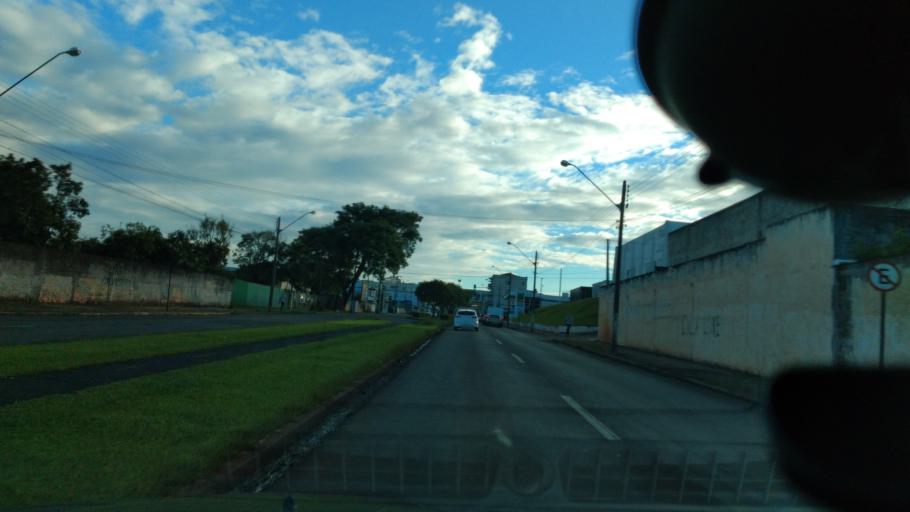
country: BR
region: Parana
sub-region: Guarapuava
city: Guarapuava
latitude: -25.3857
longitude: -51.4723
